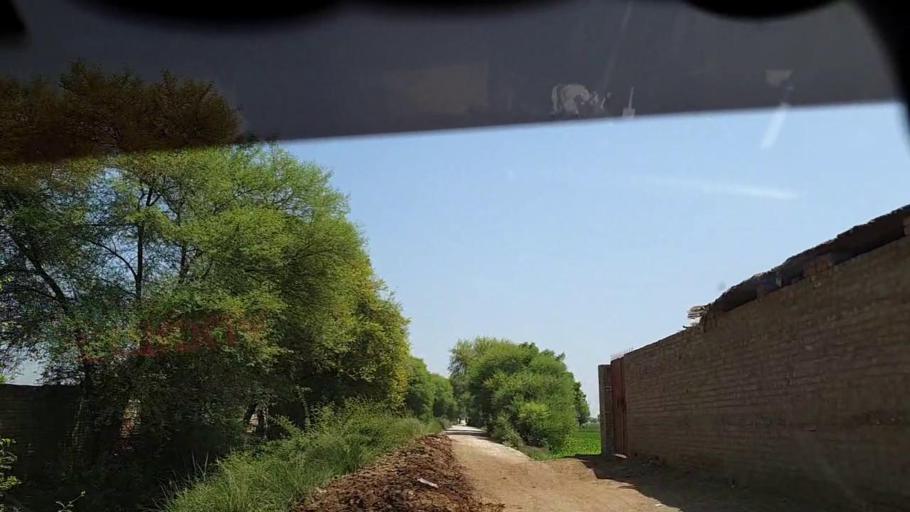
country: PK
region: Sindh
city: Ghauspur
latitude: 28.1717
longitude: 69.0604
